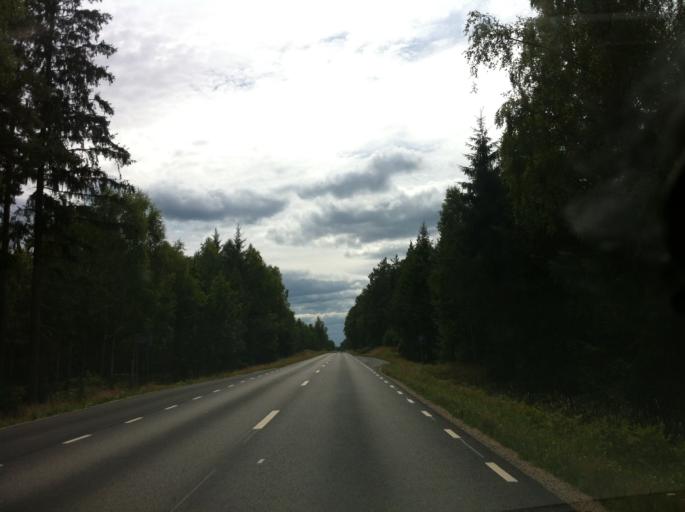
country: SE
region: Kronoberg
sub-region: Tingsryds Kommun
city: Tingsryd
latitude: 56.5384
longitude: 15.1782
